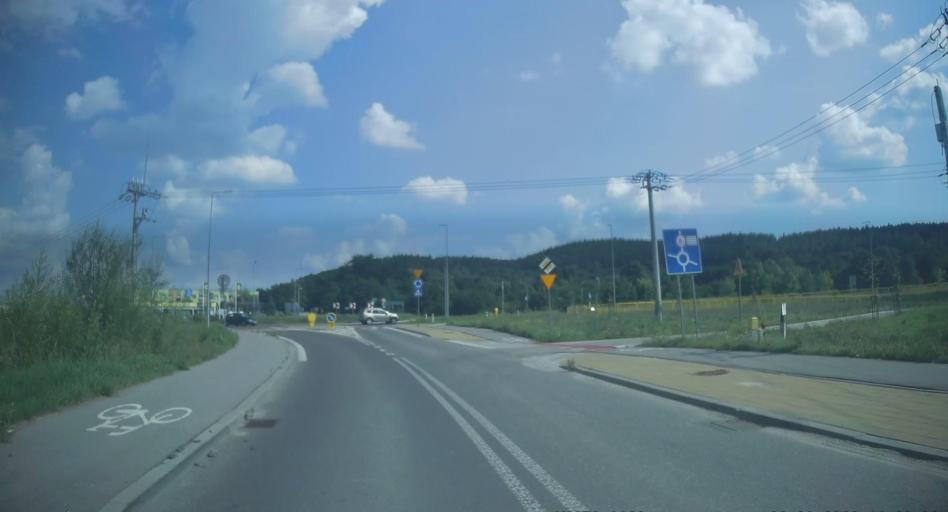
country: PL
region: Swietokrzyskie
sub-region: Powiat kielecki
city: Checiny
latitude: 50.8050
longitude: 20.4459
